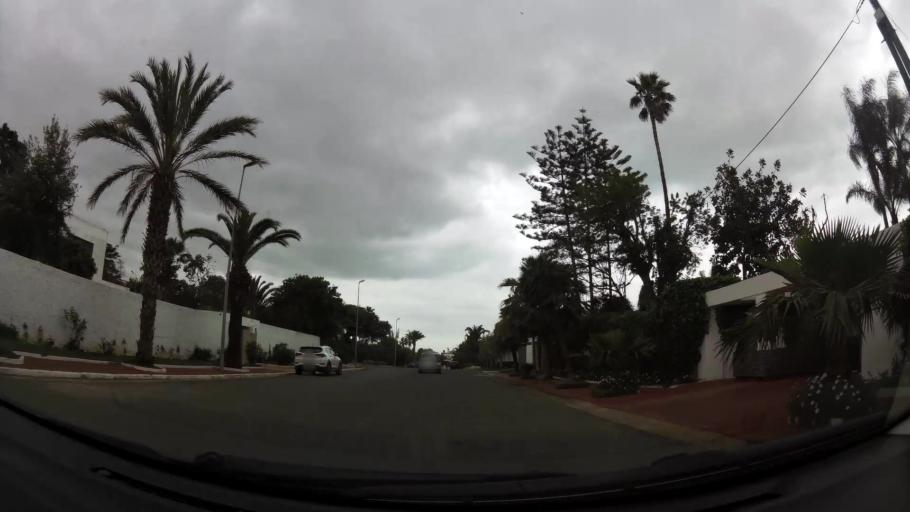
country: MA
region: Grand Casablanca
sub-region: Casablanca
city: Casablanca
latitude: 33.5827
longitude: -7.6706
